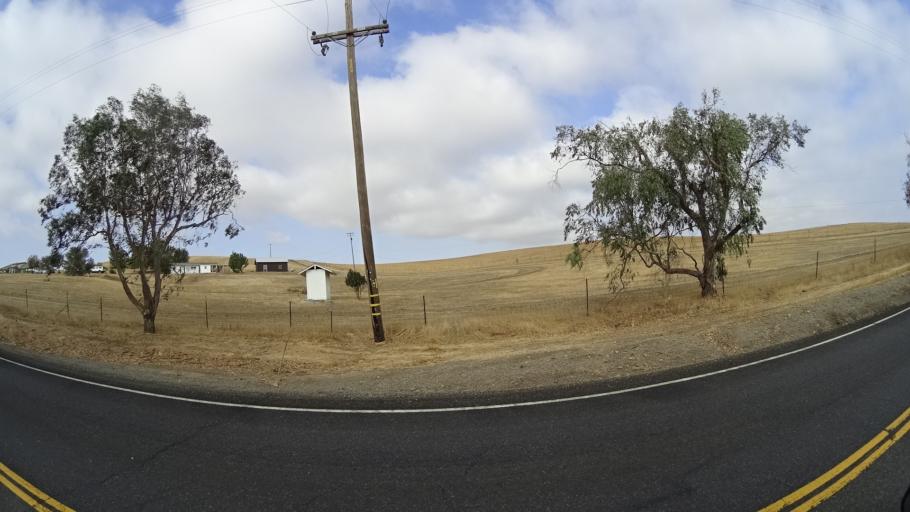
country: US
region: California
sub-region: Yolo County
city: Dunnigan
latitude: 38.7937
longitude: -121.9118
